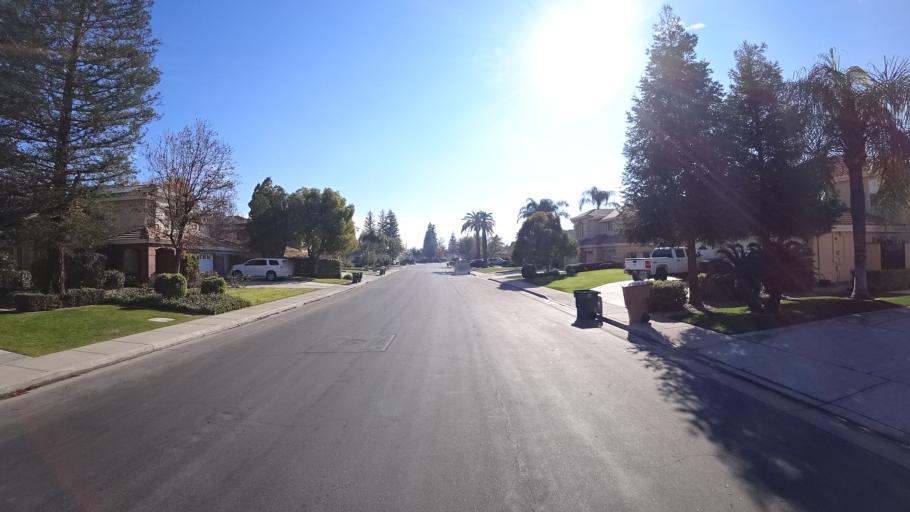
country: US
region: California
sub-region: Kern County
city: Greenacres
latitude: 35.3426
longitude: -119.1235
